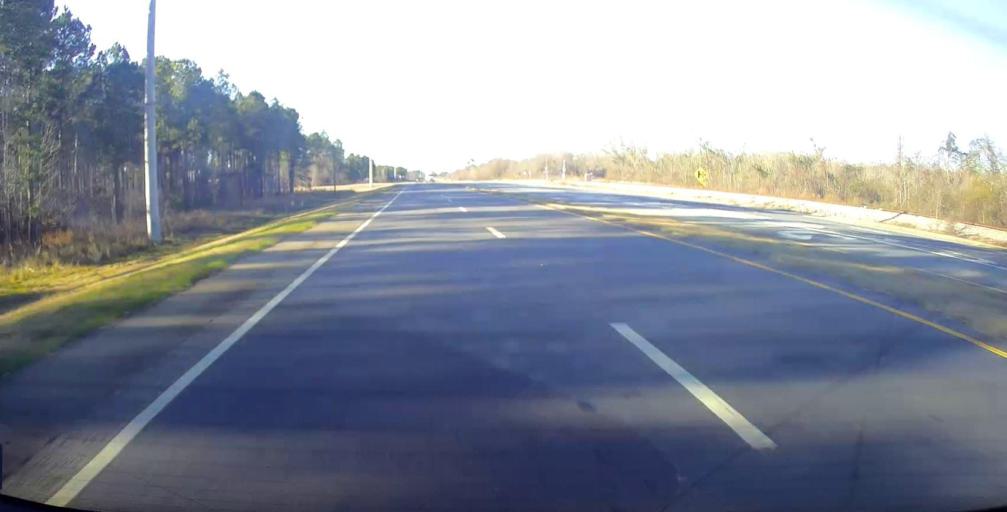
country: US
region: Georgia
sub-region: Lee County
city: Leesburg
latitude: 31.8733
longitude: -84.2393
